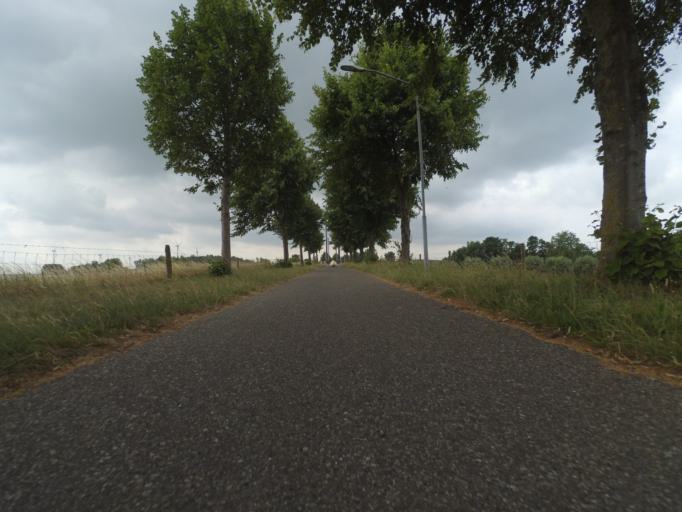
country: NL
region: North Brabant
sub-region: Gemeente Moerdijk
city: Klundert
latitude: 51.6273
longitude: 4.5870
